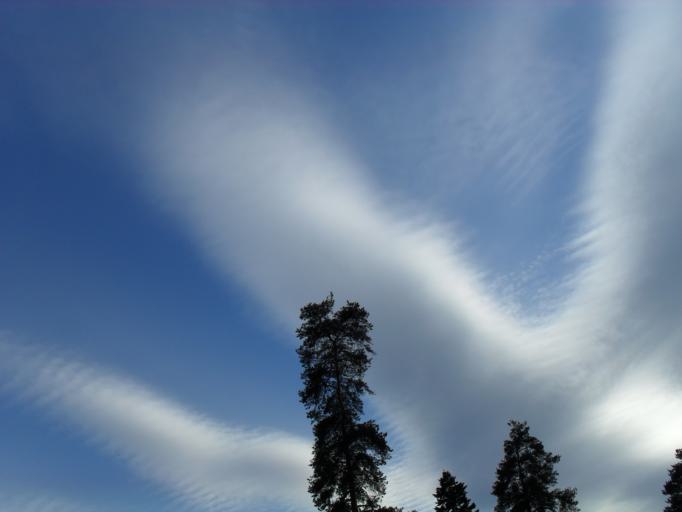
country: FI
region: Uusimaa
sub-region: Helsinki
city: Kilo
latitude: 60.2299
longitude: 24.8141
